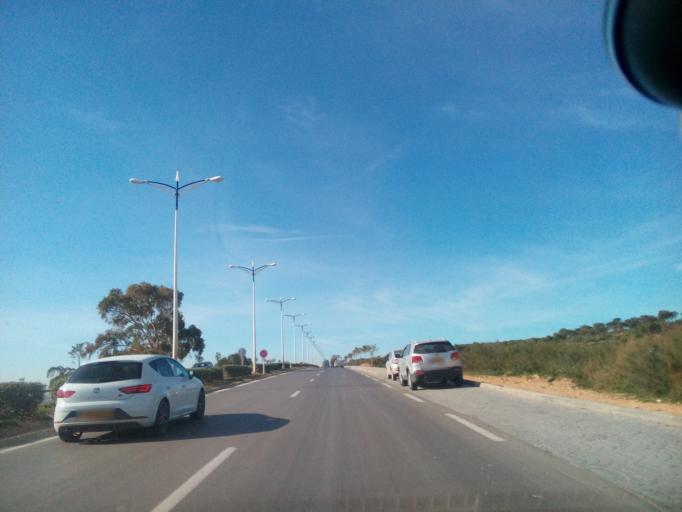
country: DZ
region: Mostaganem
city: Mostaganem
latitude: 35.9397
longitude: 0.1060
